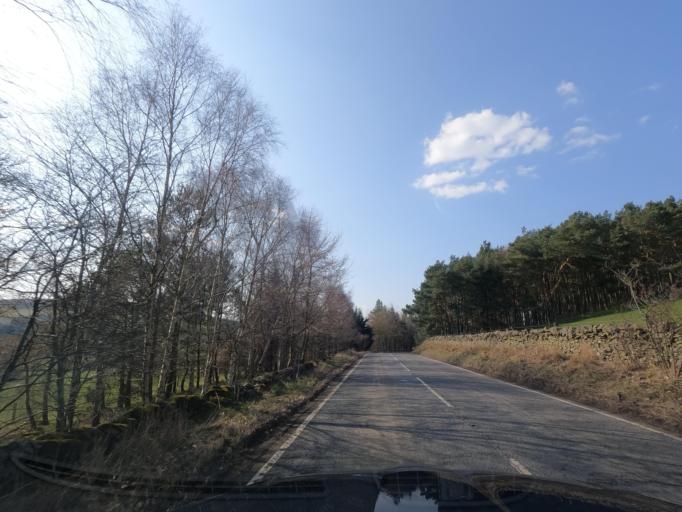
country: GB
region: Scotland
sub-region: The Scottish Borders
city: Peebles
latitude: 55.6421
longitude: -3.2424
